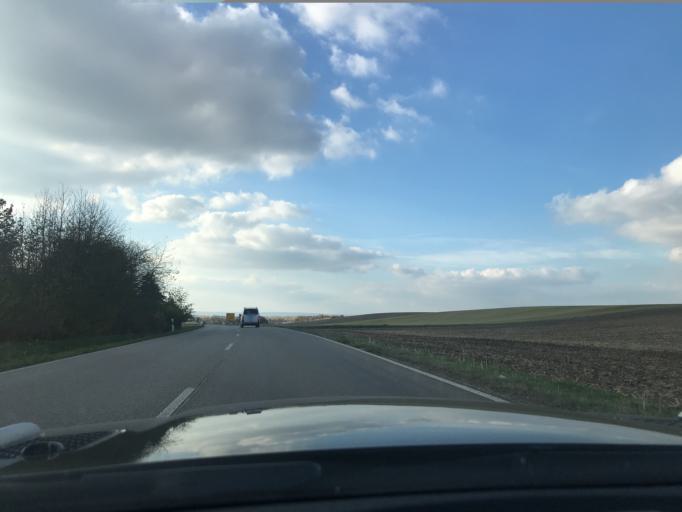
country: DE
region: Thuringia
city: Bad Langensalza
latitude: 51.1182
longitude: 10.6269
